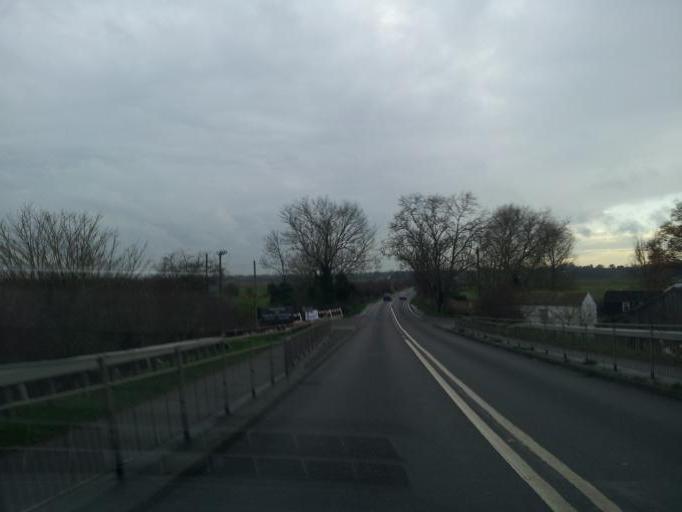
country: GB
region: England
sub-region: Norfolk
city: Acle
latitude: 52.6488
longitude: 1.5674
